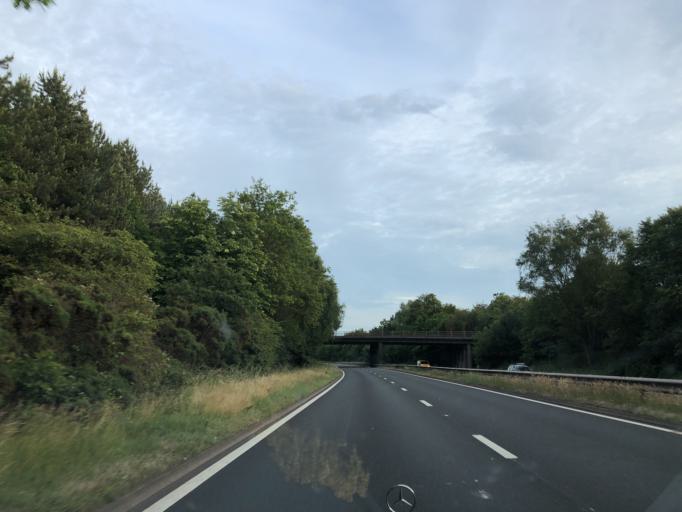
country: GB
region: England
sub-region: Solihull
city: Bickenhill
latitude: 52.4611
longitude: -1.7028
